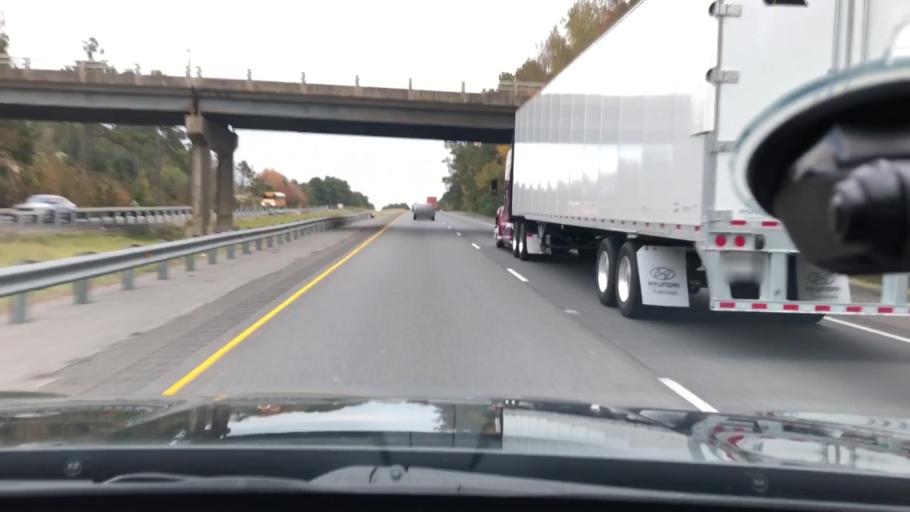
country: US
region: Arkansas
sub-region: Clark County
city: Arkadelphia
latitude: 34.2348
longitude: -93.0078
